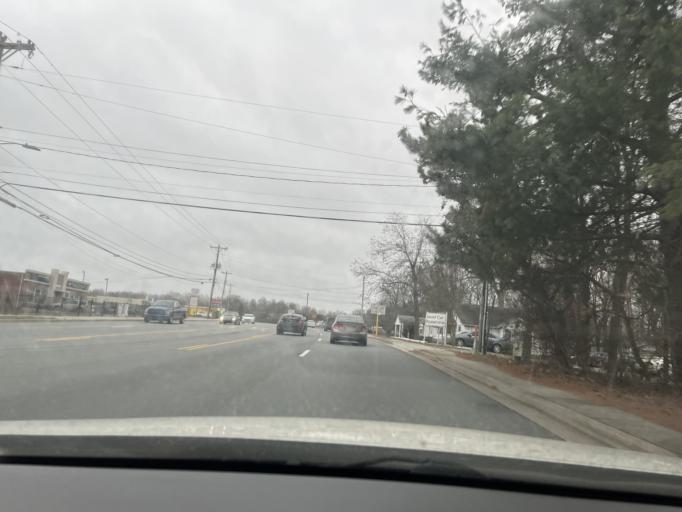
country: US
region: North Carolina
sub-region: Guilford County
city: Greensboro
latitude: 36.0266
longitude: -79.8026
